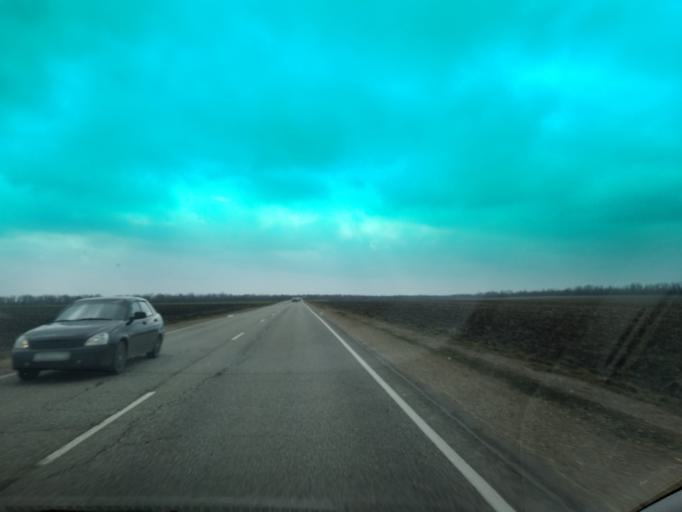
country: RU
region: Krasnodarskiy
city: Novomalorossiyskaya
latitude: 45.7357
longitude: 39.9109
